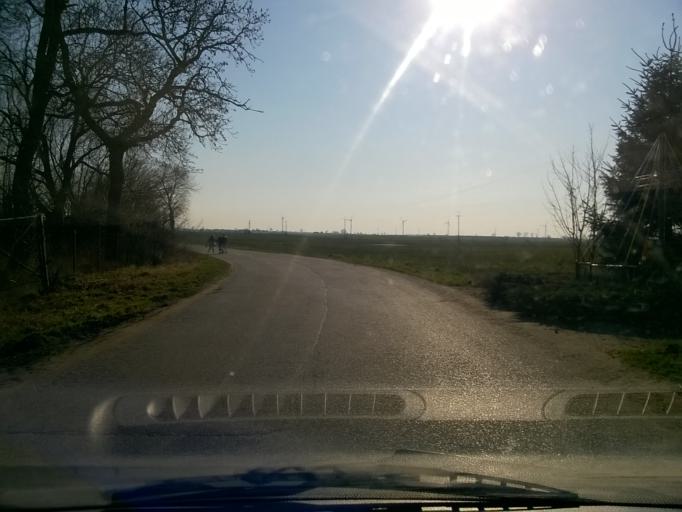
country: PL
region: Greater Poland Voivodeship
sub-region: Powiat wagrowiecki
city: Golancz
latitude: 52.9818
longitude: 17.3390
